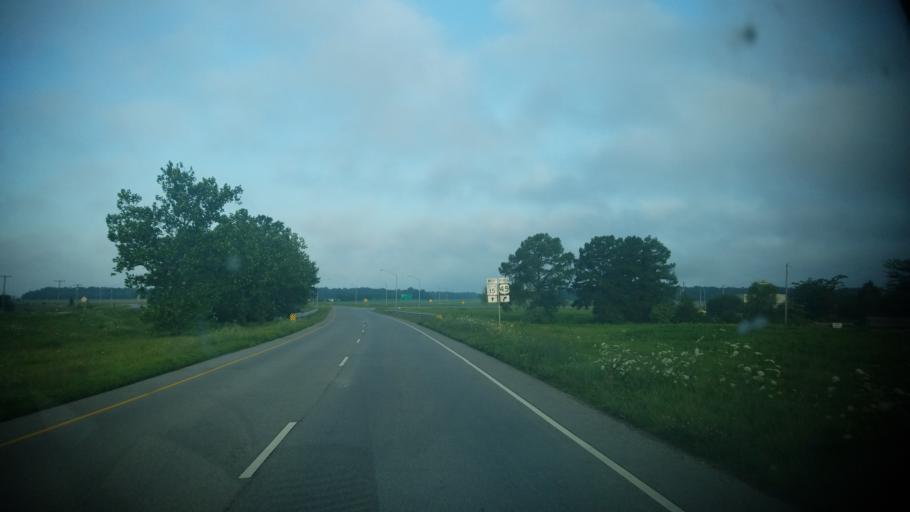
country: US
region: Illinois
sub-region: Wayne County
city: Fairfield
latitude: 38.3795
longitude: -88.4014
